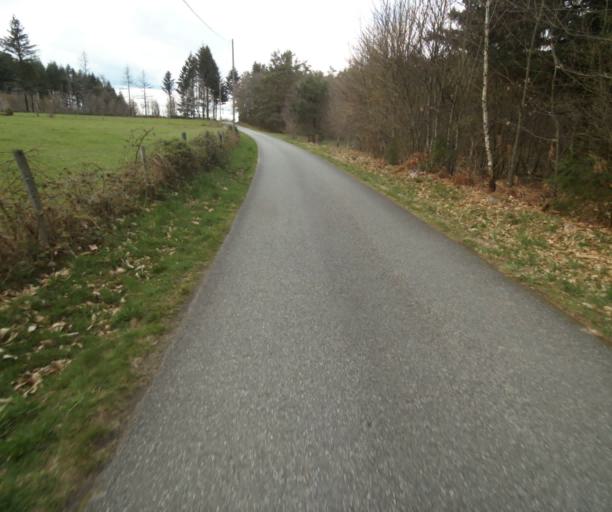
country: FR
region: Limousin
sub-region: Departement de la Correze
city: Correze
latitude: 45.2988
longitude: 1.9220
